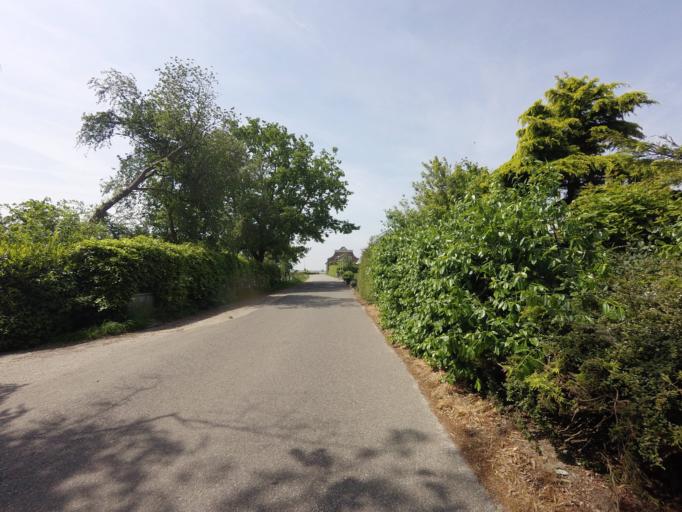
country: NL
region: South Holland
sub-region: Gemeente Hellevoetsluis
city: Nieuwenhoorn
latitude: 51.8260
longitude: 4.1772
